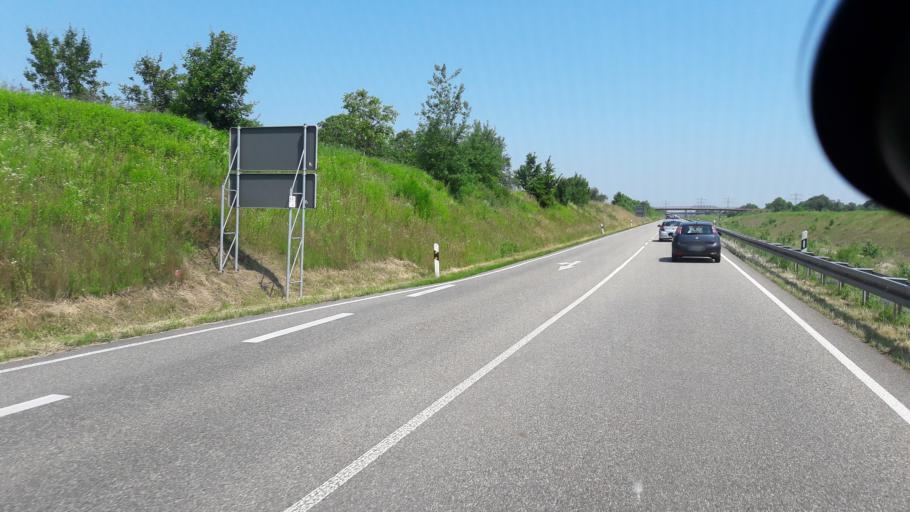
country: DE
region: Baden-Wuerttemberg
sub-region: Karlsruhe Region
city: Otigheim
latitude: 48.8880
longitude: 8.2495
